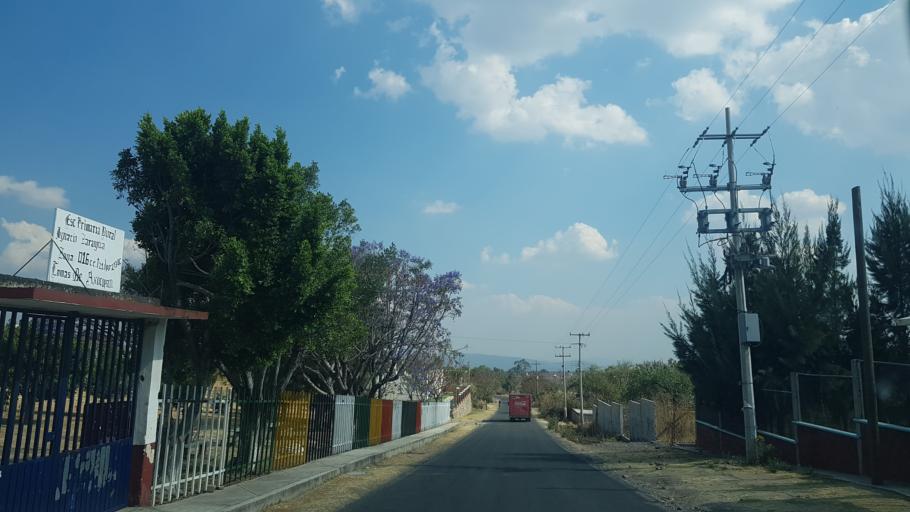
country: MX
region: Puebla
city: Atlixco
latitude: 18.9155
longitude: -98.4794
